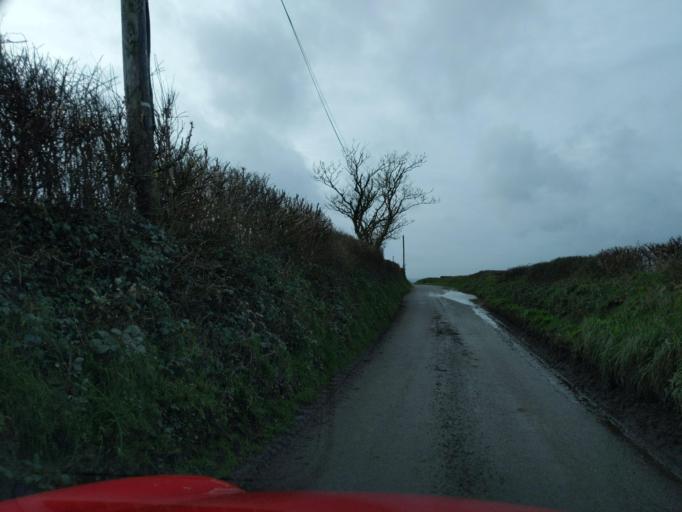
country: GB
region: England
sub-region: Cornwall
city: Fowey
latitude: 50.3437
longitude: -4.5650
